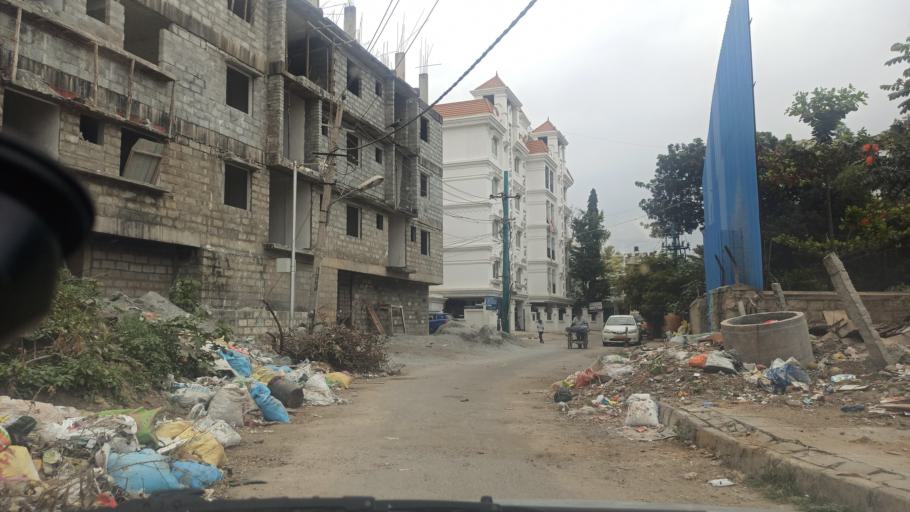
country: IN
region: Karnataka
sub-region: Bangalore Urban
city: Yelahanka
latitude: 13.0371
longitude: 77.6016
